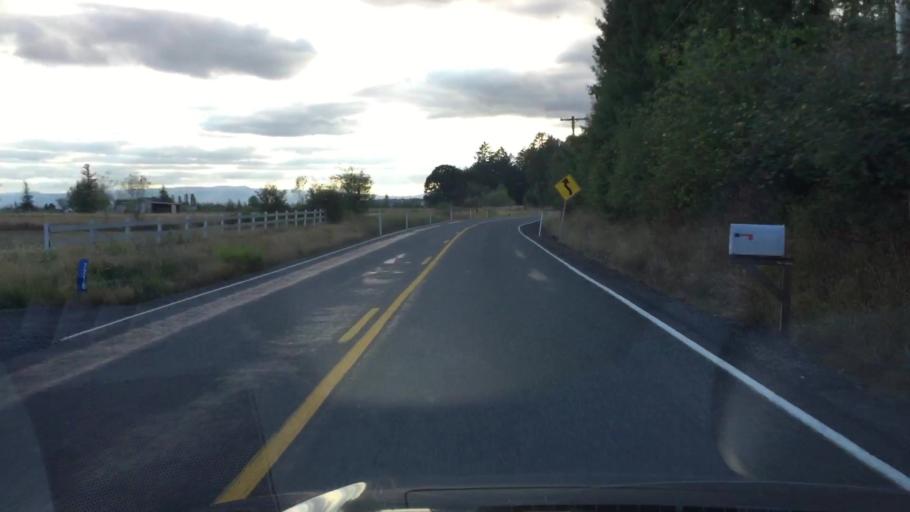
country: US
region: Washington
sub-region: Lewis County
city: Napavine
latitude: 46.4935
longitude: -122.7735
